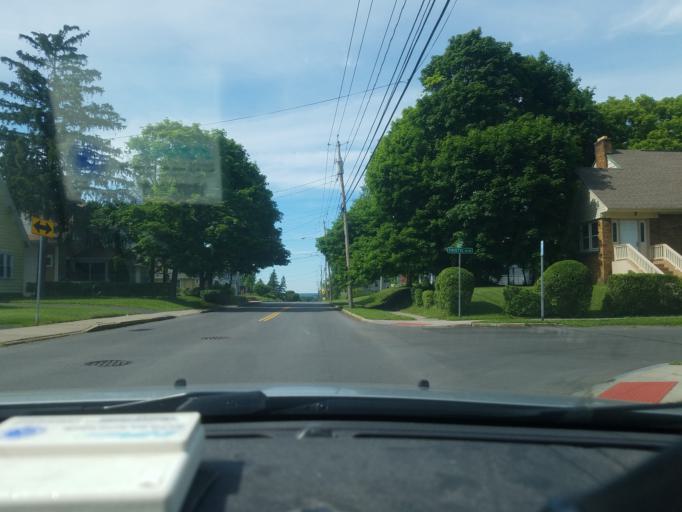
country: US
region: New York
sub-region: Onondaga County
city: East Syracuse
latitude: 43.0488
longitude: -76.1037
